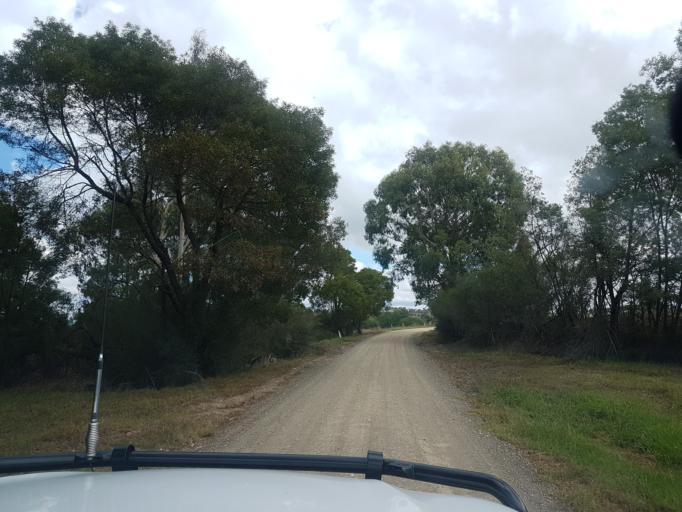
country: AU
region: Victoria
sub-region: East Gippsland
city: Bairnsdale
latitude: -37.7852
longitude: 147.5483
